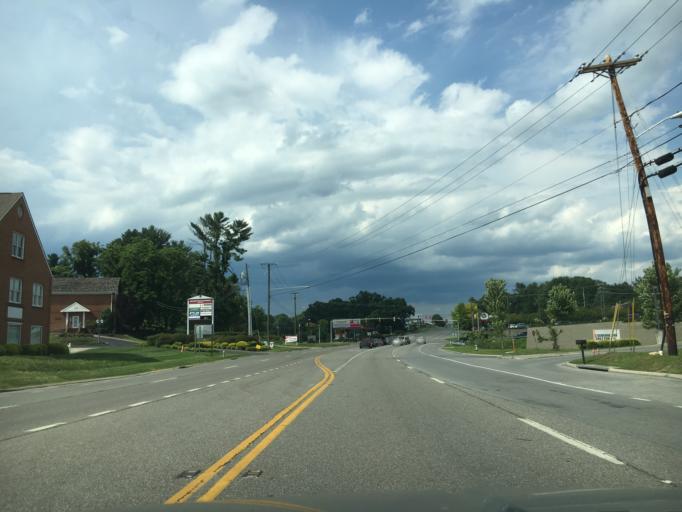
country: US
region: Virginia
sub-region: Roanoke County
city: Cave Spring
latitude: 37.2226
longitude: -80.0143
